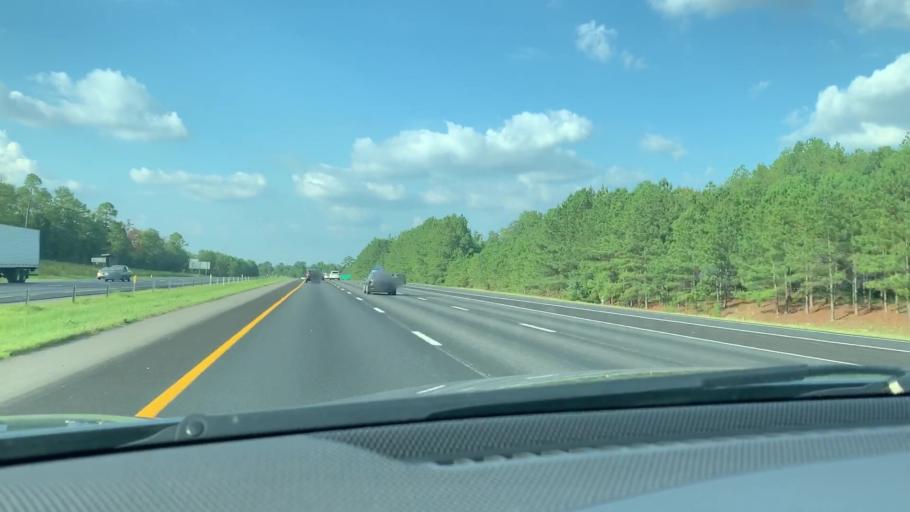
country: US
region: South Carolina
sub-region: Richland County
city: Forest Acres
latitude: 33.9824
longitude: -80.9537
